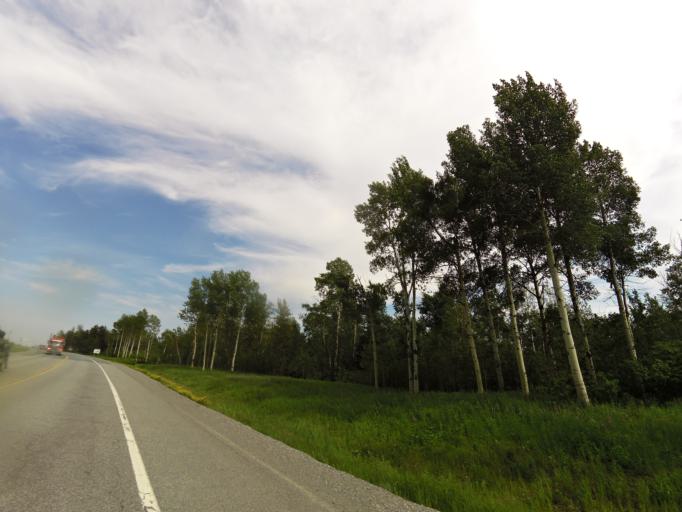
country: CA
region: Quebec
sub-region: Abitibi-Temiscamingue
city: Malartic
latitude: 48.2263
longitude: -78.3955
